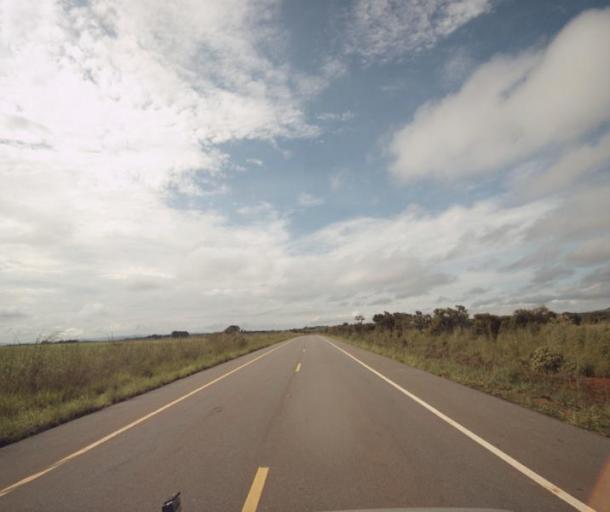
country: BR
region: Goias
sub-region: Padre Bernardo
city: Padre Bernardo
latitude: -15.3277
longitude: -48.6526
